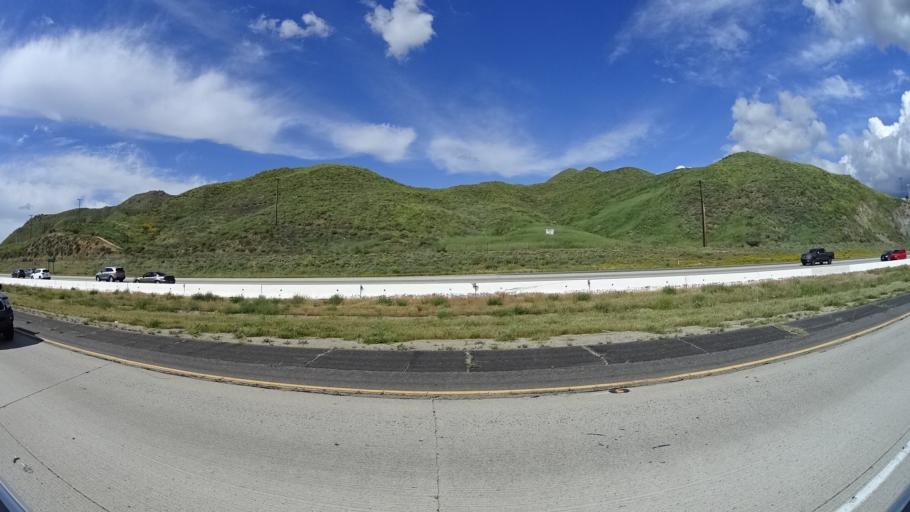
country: US
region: California
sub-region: Riverside County
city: Lake Elsinore
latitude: 33.7326
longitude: -117.4041
